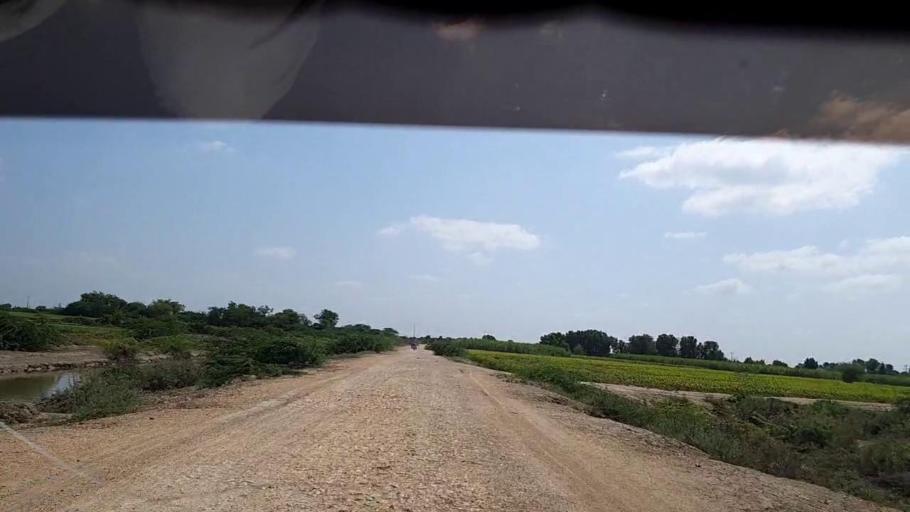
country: PK
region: Sindh
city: Kadhan
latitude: 24.5923
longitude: 68.9920
